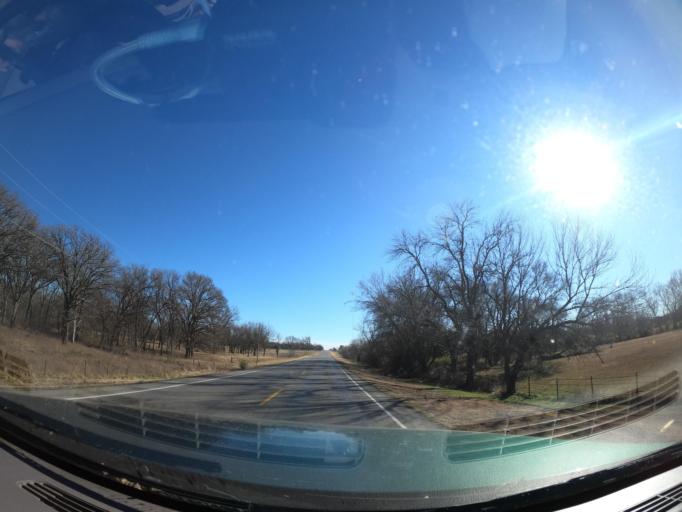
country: US
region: Oklahoma
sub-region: Muskogee County
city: Haskell
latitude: 35.7729
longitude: -95.6555
